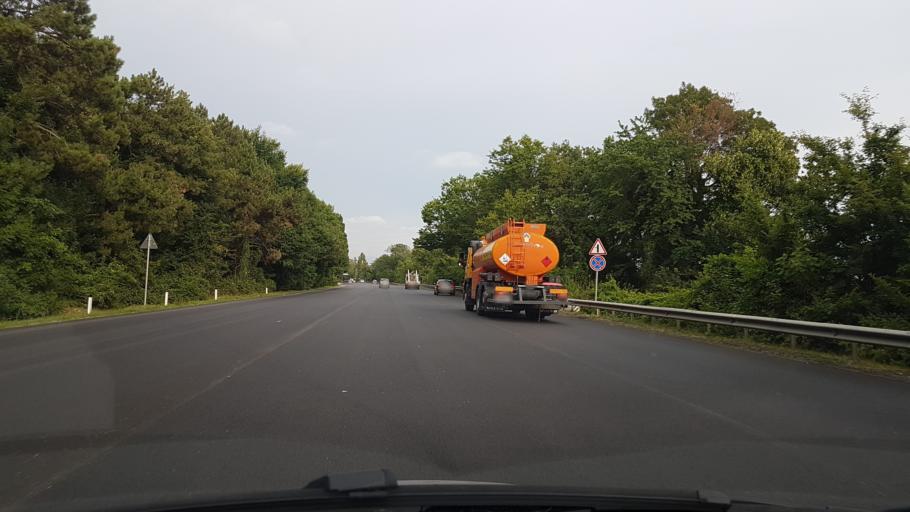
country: RU
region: Krasnodarskiy
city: Lermontovo
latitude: 44.2880
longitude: 38.7778
